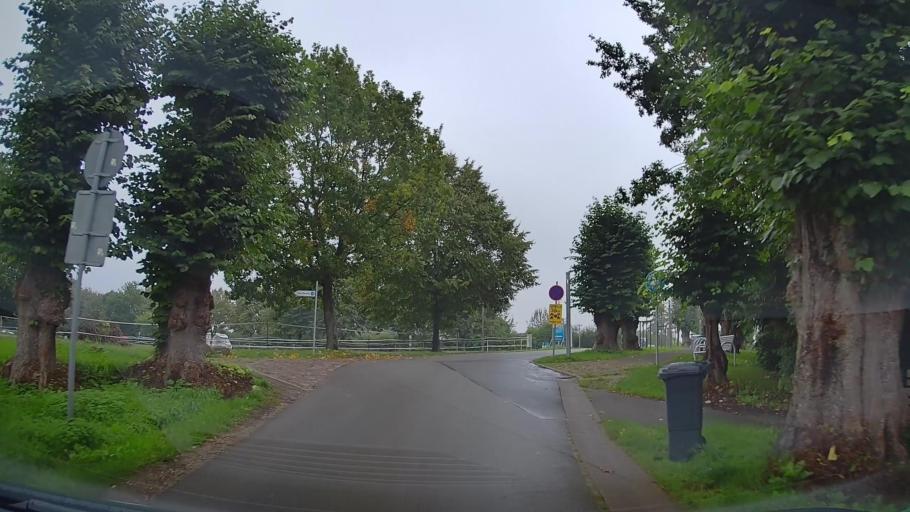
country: DE
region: Mecklenburg-Vorpommern
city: Gramkow
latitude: 53.9283
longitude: 11.3697
